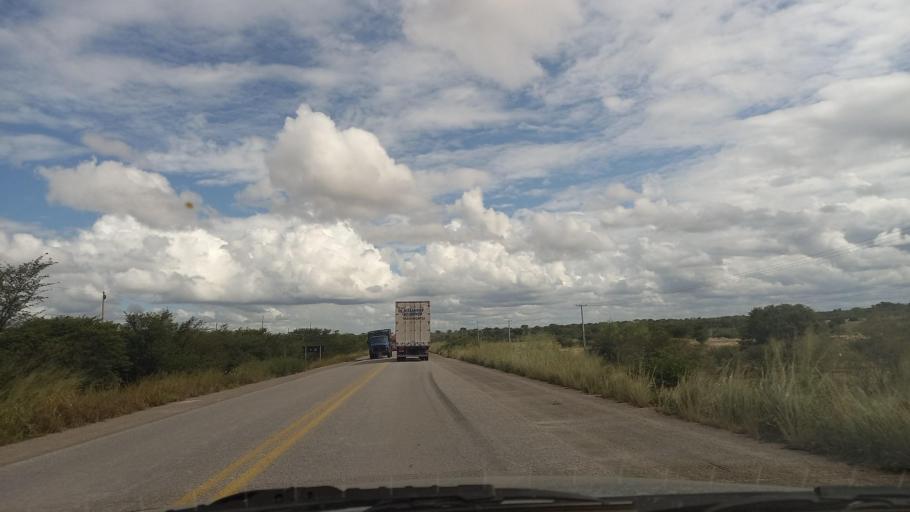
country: BR
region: Pernambuco
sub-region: Cachoeirinha
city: Cachoeirinha
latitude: -8.4079
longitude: -36.1875
